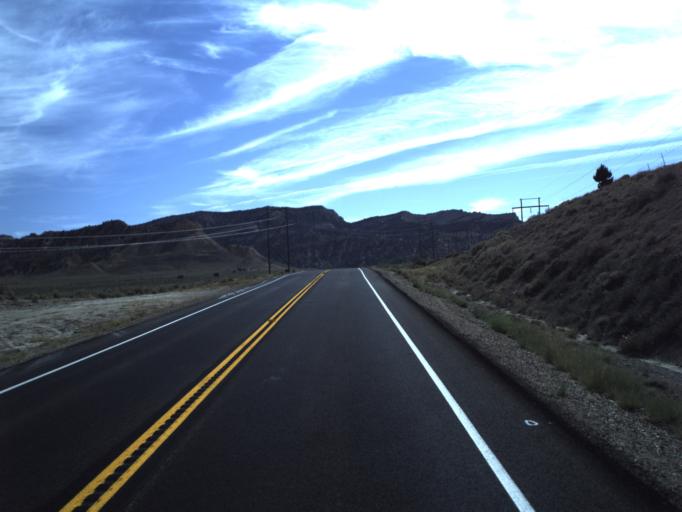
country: US
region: Utah
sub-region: Garfield County
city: Panguitch
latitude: 37.6022
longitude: -111.9607
